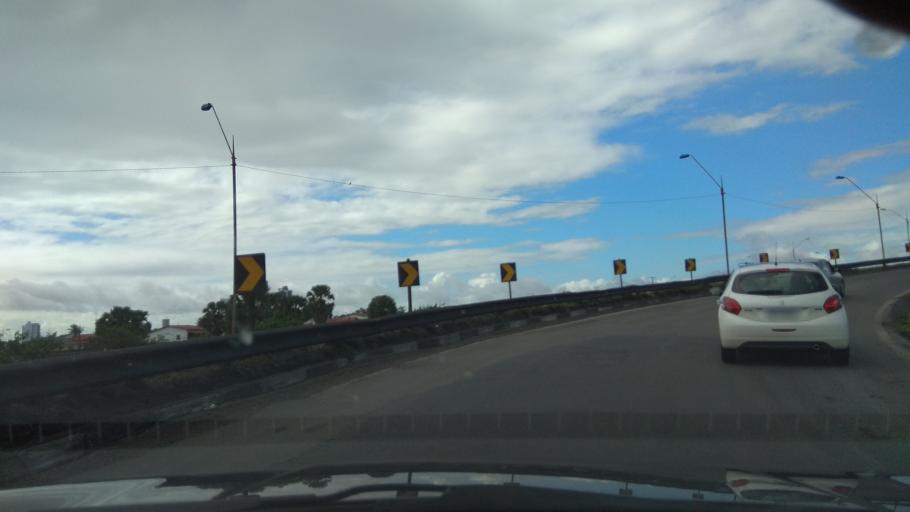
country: BR
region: Bahia
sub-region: Feira De Santana
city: Feira de Santana
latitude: -12.2713
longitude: -38.9362
